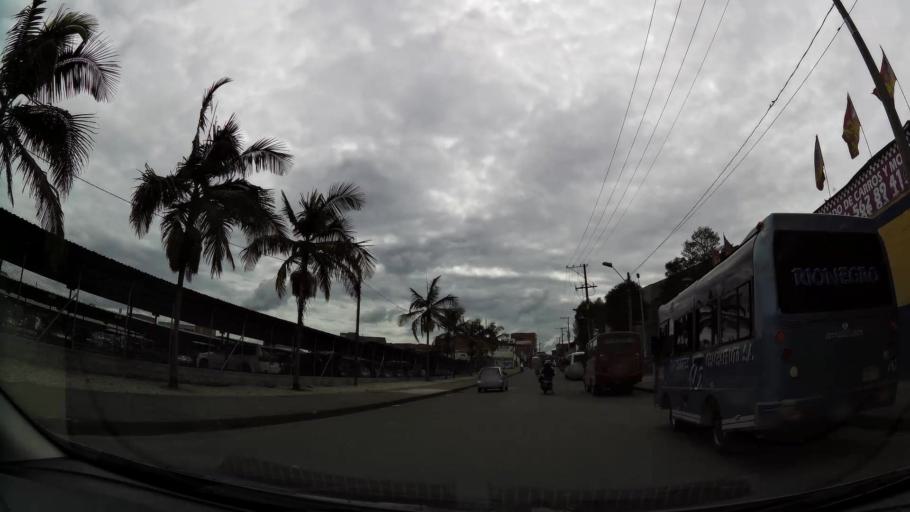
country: CO
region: Antioquia
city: Rionegro
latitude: 6.1523
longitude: -75.3725
